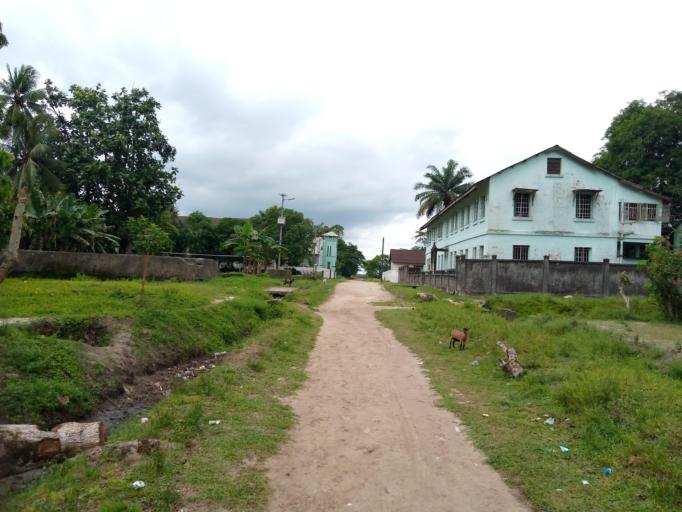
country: SL
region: Southern Province
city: Bonthe
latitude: 7.5314
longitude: -12.5044
